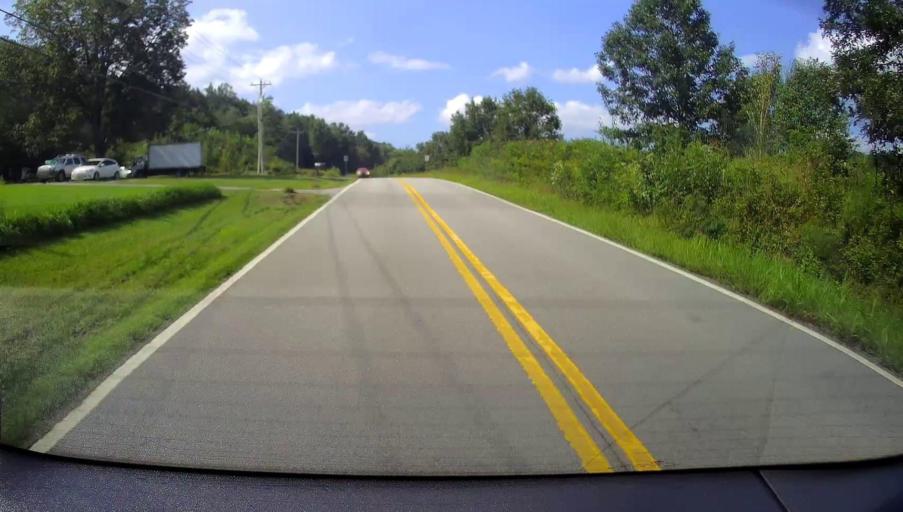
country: US
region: Georgia
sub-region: Catoosa County
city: Ringgold
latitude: 34.9279
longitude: -85.0853
